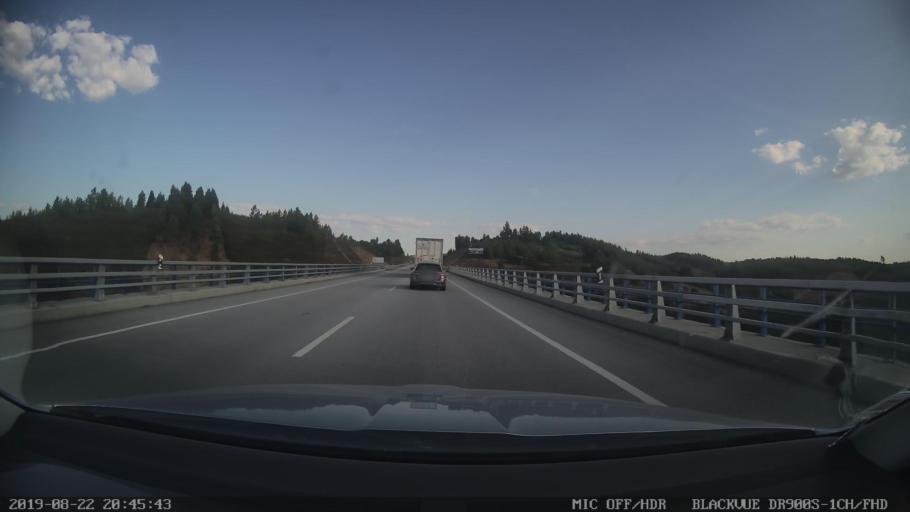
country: PT
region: Castelo Branco
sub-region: Proenca-A-Nova
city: Proenca-a-Nova
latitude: 39.7197
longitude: -7.8693
